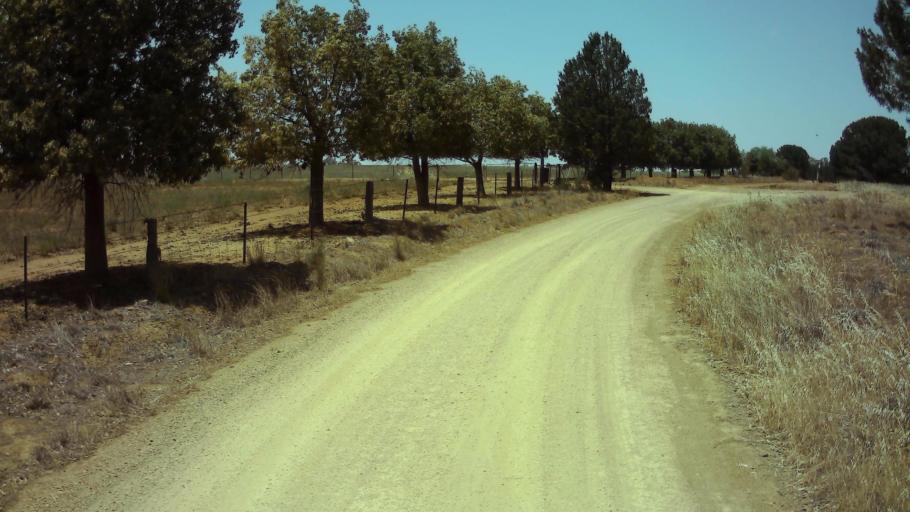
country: AU
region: New South Wales
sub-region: Weddin
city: Grenfell
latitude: -33.9112
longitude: 148.1648
